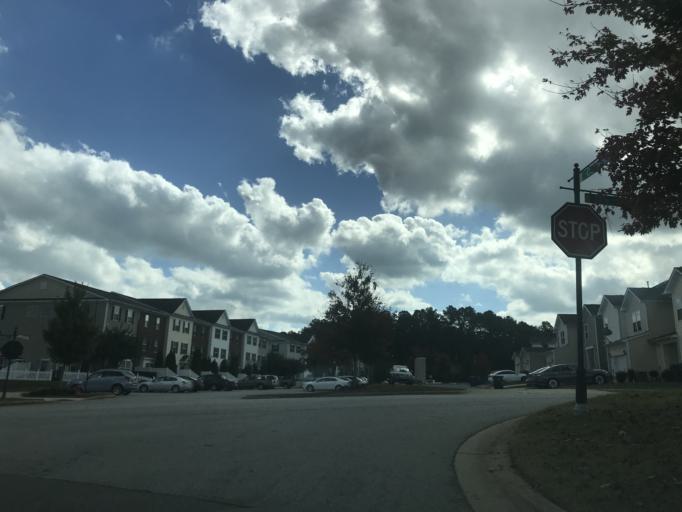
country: US
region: North Carolina
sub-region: Wake County
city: Raleigh
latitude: 35.7385
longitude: -78.6537
